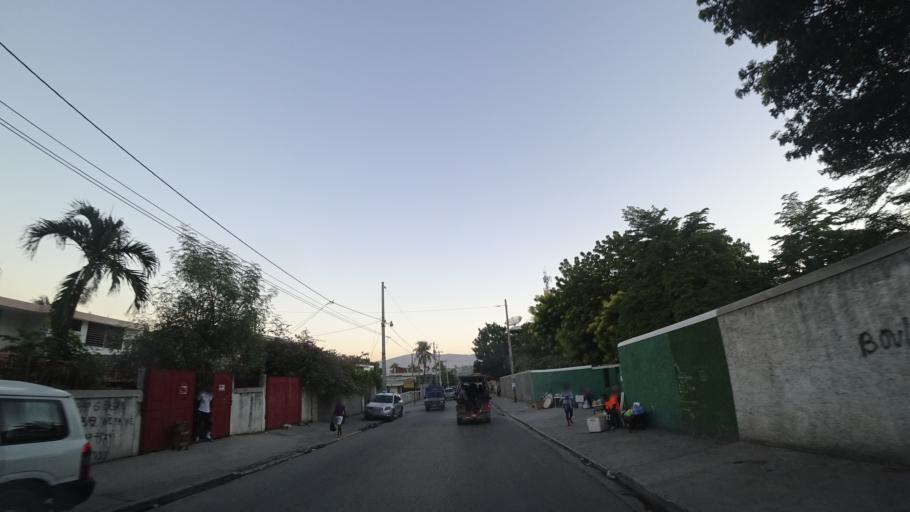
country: HT
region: Ouest
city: Delmas 73
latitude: 18.5545
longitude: -72.3043
